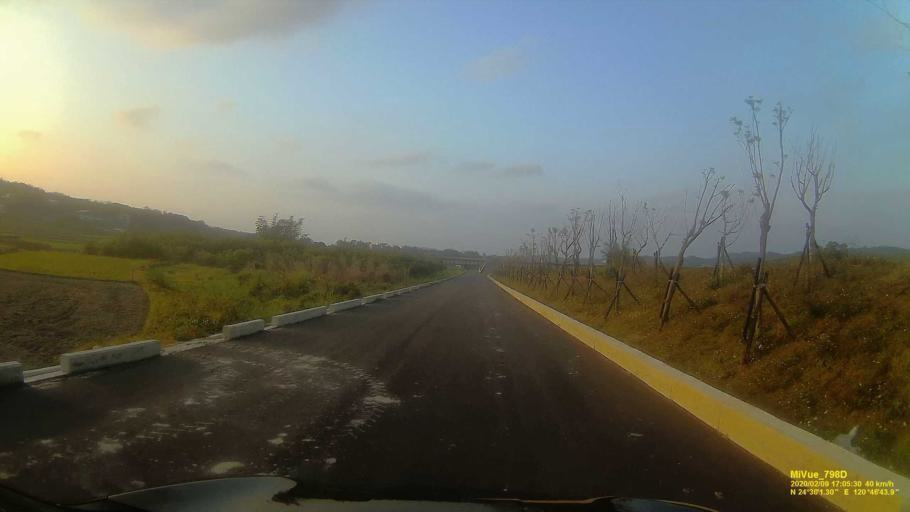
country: TW
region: Taiwan
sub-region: Miaoli
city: Miaoli
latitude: 24.5006
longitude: 120.7788
